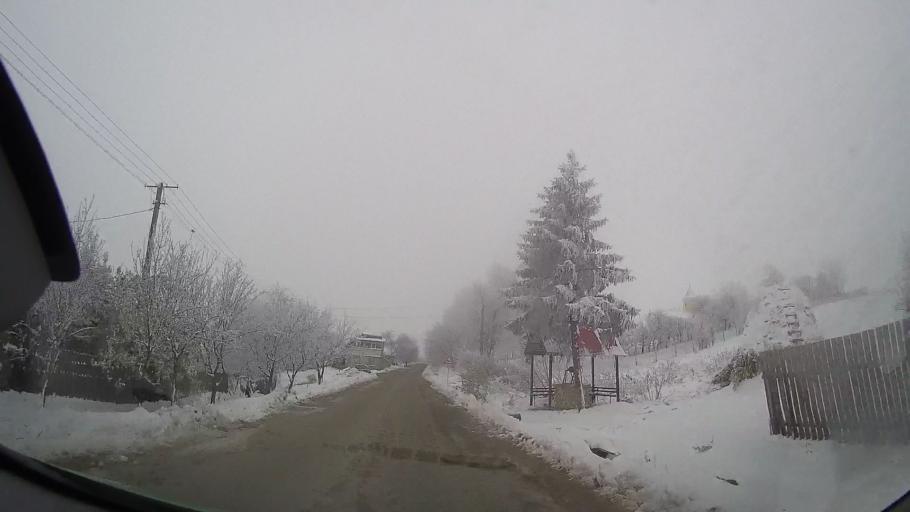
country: RO
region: Iasi
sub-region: Comuna Dagata
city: Dagata
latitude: 46.9205
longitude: 27.1673
